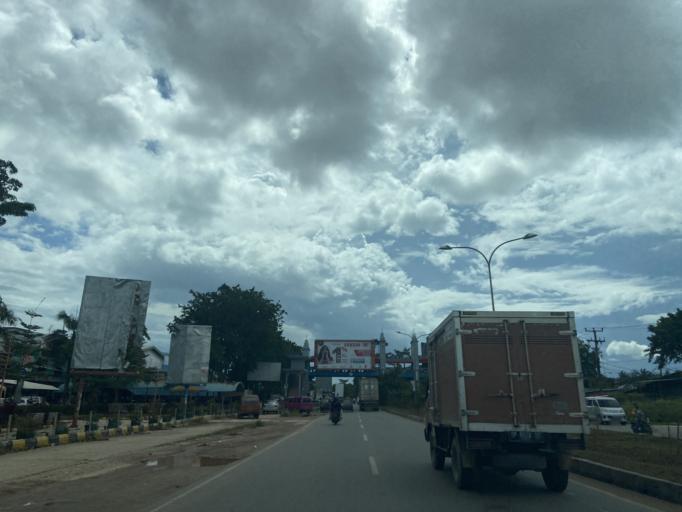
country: SG
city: Singapore
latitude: 1.0416
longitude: 103.9836
